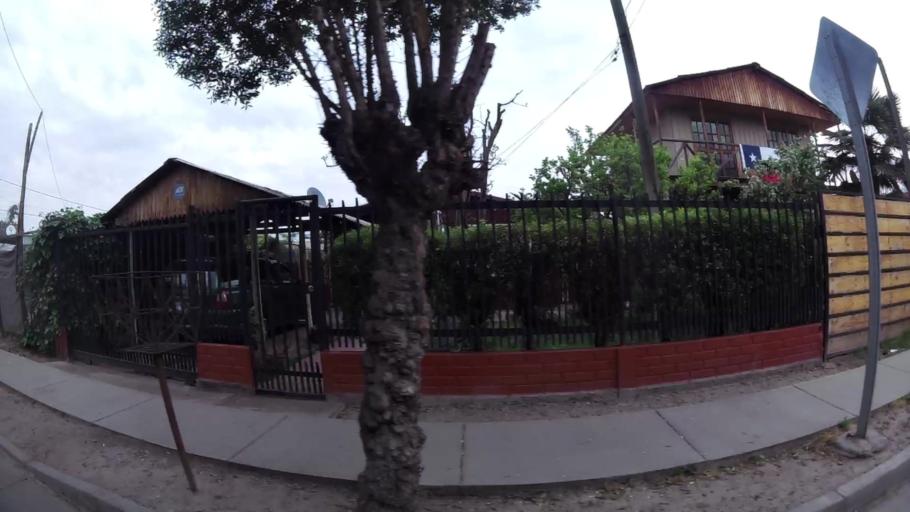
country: CL
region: Santiago Metropolitan
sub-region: Provincia de Chacabuco
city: Lampa
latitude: -33.2271
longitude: -70.8082
